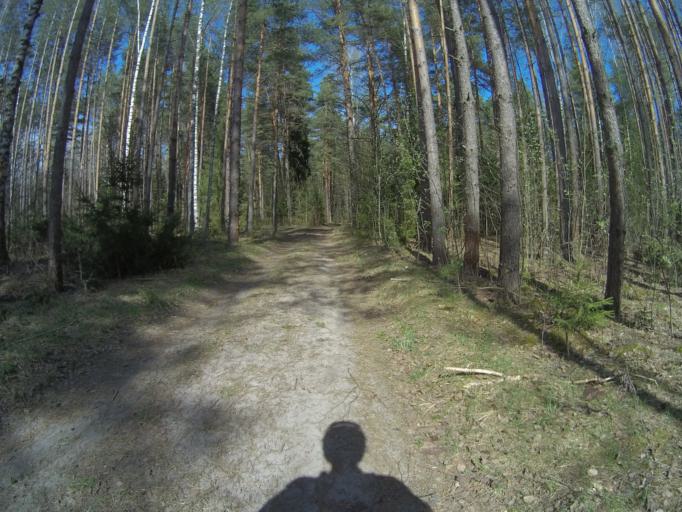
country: RU
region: Vladimir
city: Bogolyubovo
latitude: 56.1244
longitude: 40.5380
